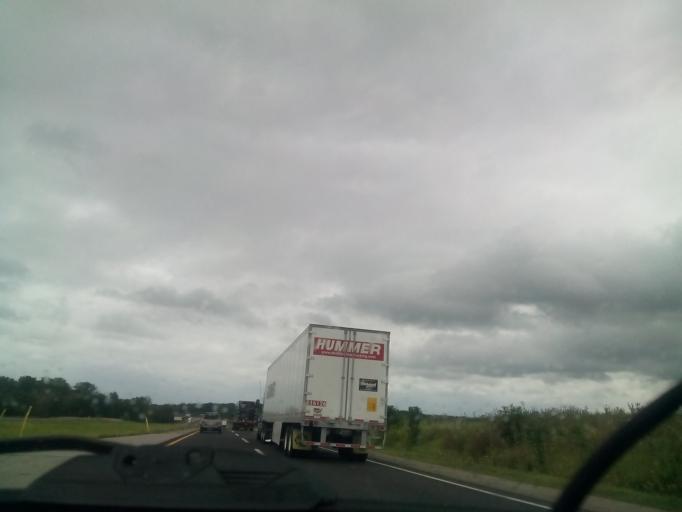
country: US
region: Indiana
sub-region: Steuben County
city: Hamilton
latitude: 41.6356
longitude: -84.8246
